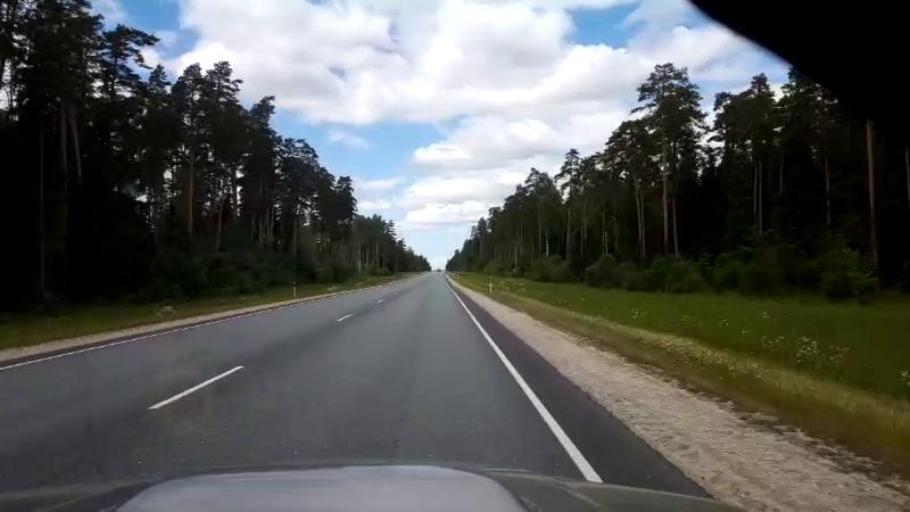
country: EE
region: Raplamaa
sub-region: Maerjamaa vald
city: Marjamaa
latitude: 59.0072
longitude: 24.4581
